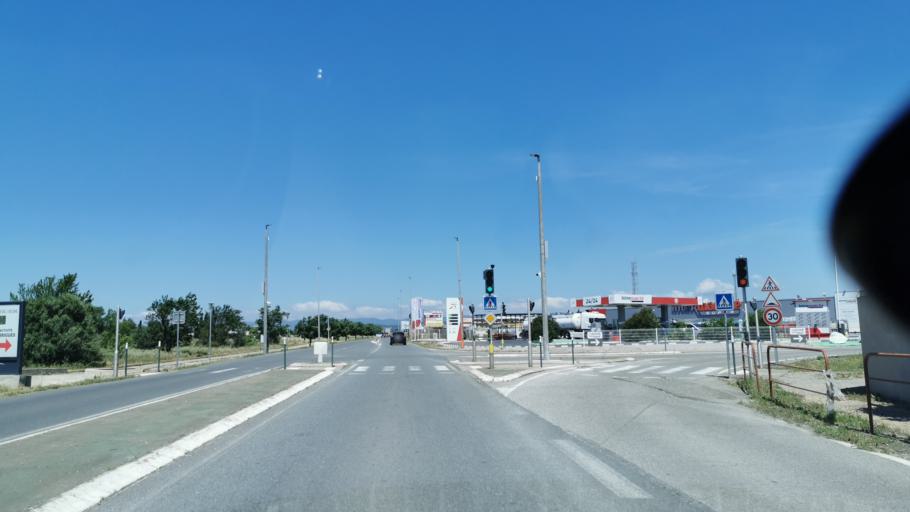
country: FR
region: Languedoc-Roussillon
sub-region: Departement de l'Aude
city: Saint-Marcel-sur-Aude
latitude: 43.2531
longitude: 2.9133
